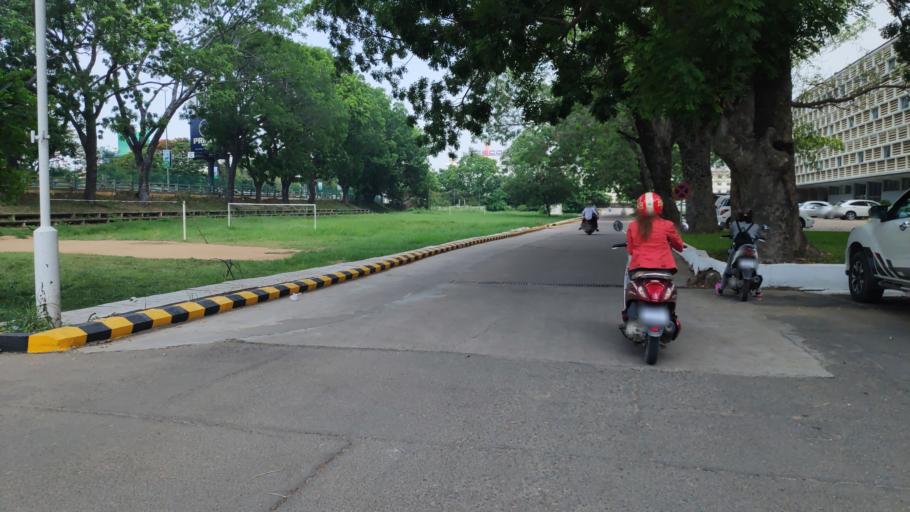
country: KH
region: Phnom Penh
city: Phnom Penh
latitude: 11.5700
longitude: 104.8981
